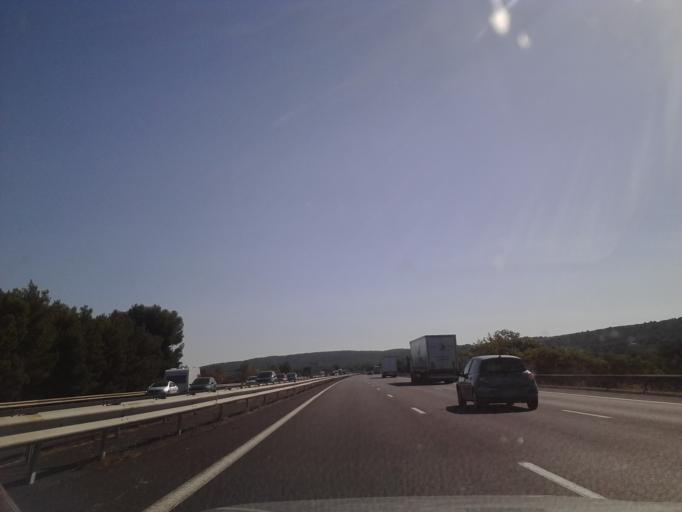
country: FR
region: Languedoc-Roussillon
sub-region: Departement de l'Aude
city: Vinassan
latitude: 43.1825
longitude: 3.0485
